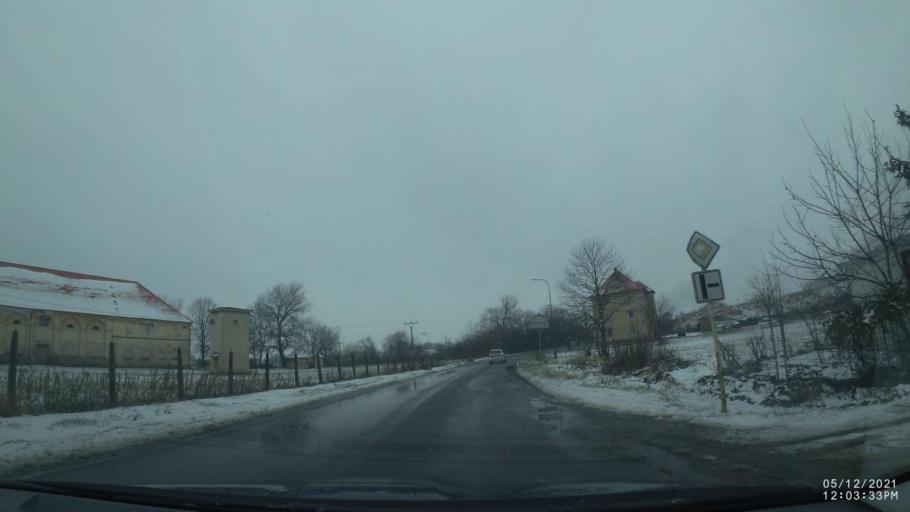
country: CZ
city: Ceske Mezirici
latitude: 50.2831
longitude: 16.0585
